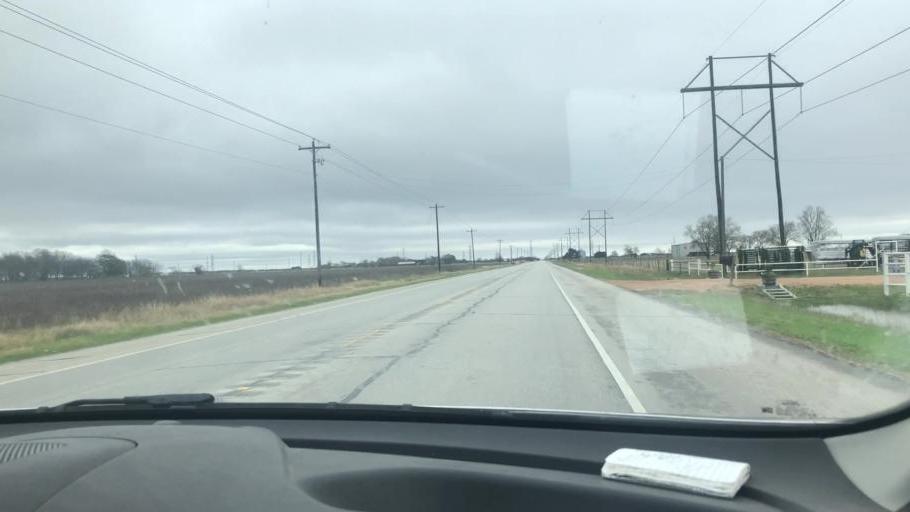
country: US
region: Texas
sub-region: Wharton County
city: Boling
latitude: 29.1893
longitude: -96.0136
